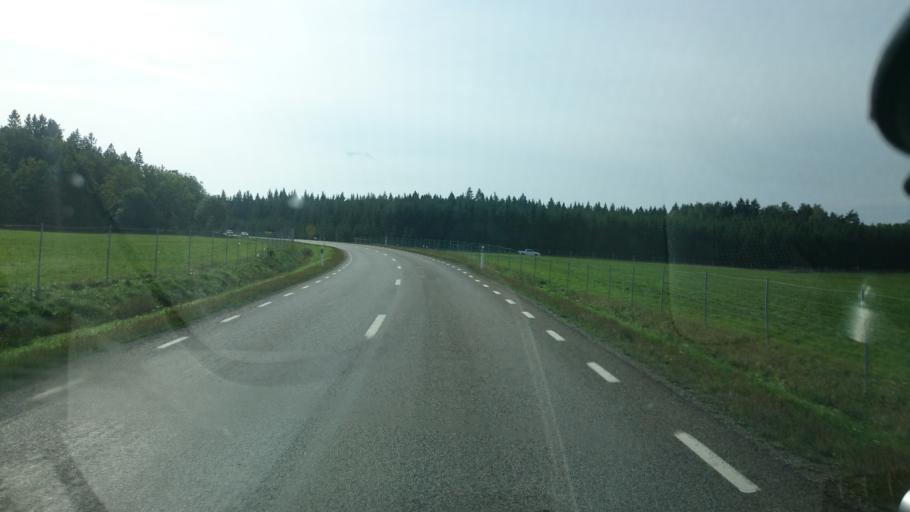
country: SE
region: Vaestra Goetaland
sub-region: Alingsas Kommun
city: Sollebrunn
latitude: 58.1490
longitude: 12.4173
